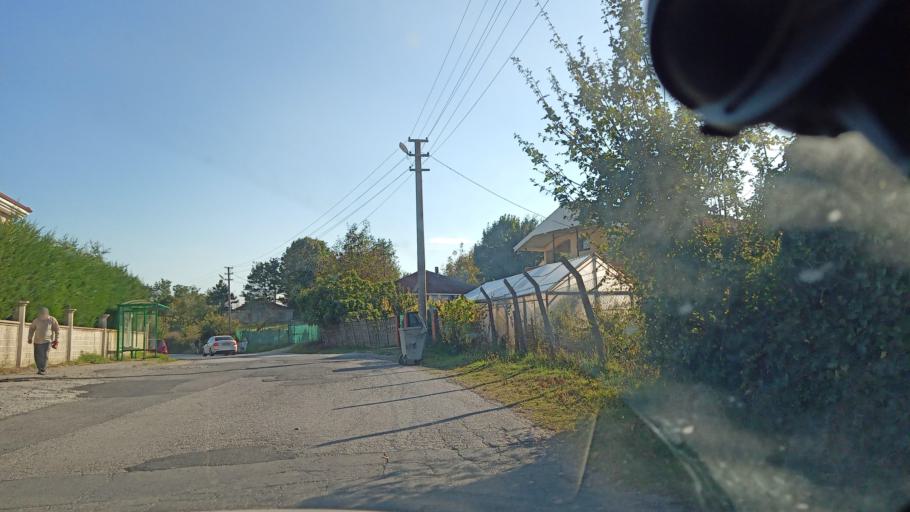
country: TR
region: Sakarya
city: Kazimpasa
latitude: 40.8566
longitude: 30.2852
